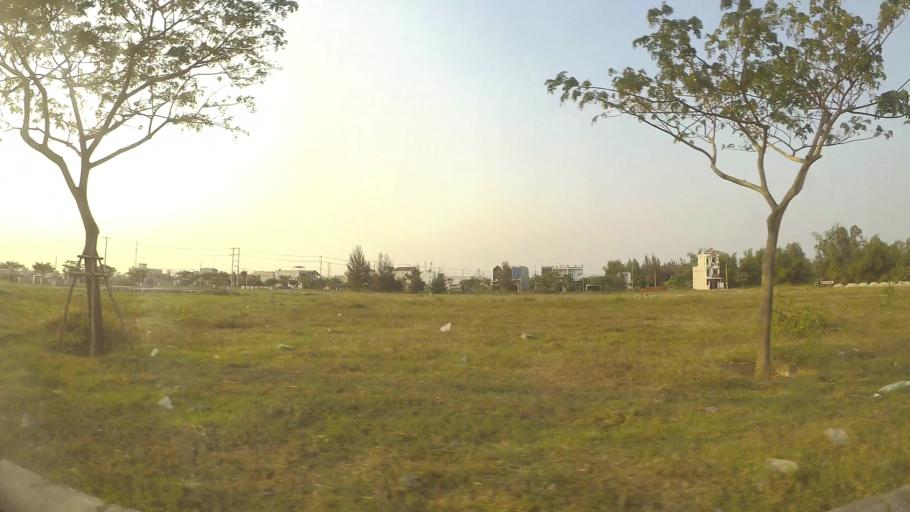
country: VN
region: Da Nang
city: Ngu Hanh Son
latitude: 15.9770
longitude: 108.2346
